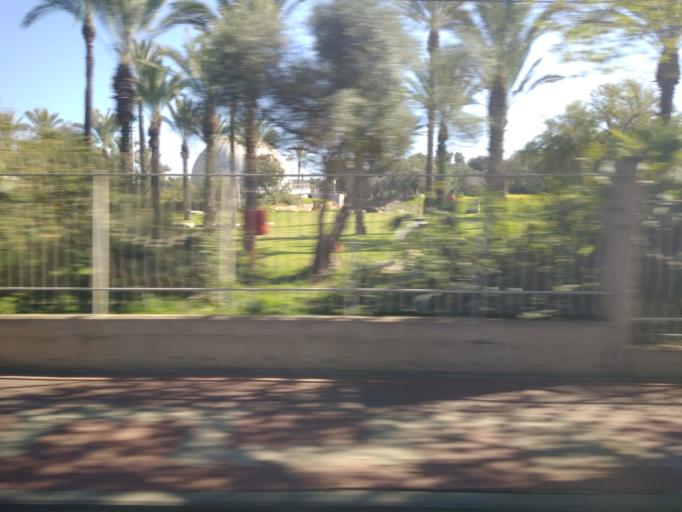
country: IL
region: Tel Aviv
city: Tel Aviv
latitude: 32.1021
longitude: 34.7931
